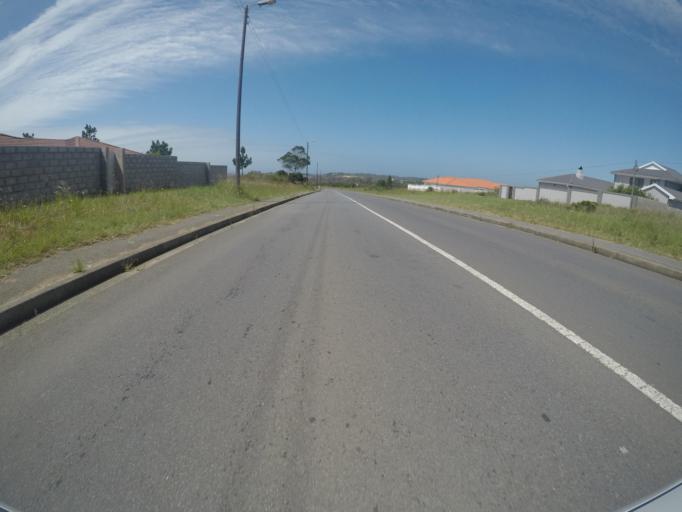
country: ZA
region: Eastern Cape
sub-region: Buffalo City Metropolitan Municipality
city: East London
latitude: -32.9418
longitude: 27.9940
